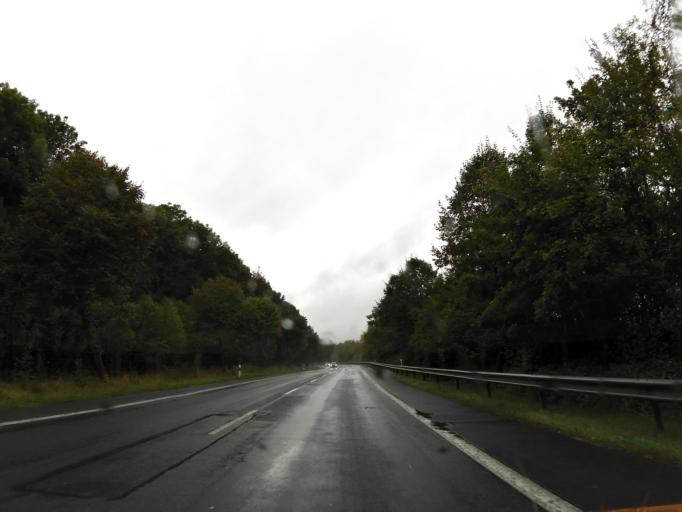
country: DE
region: Lower Saxony
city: Waake
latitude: 51.5612
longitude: 10.0255
